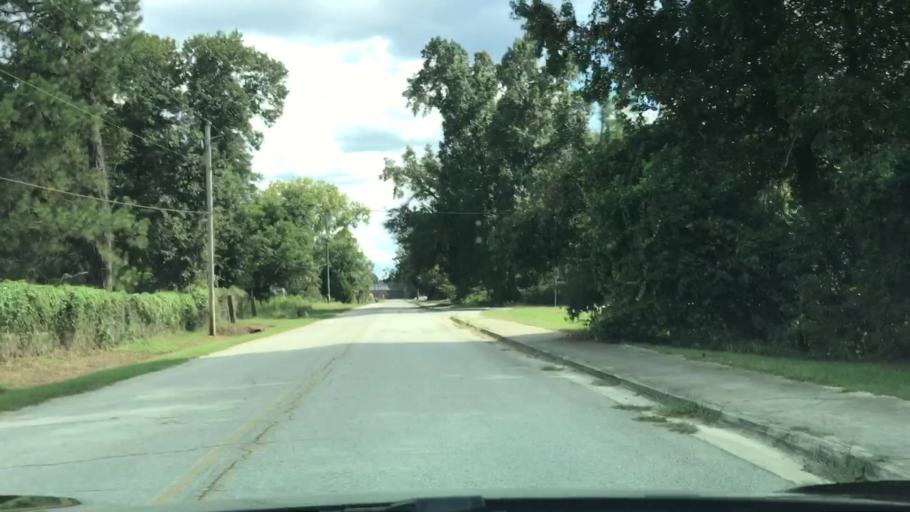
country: US
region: Georgia
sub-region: Jefferson County
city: Wadley
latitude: 32.8604
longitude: -82.3970
